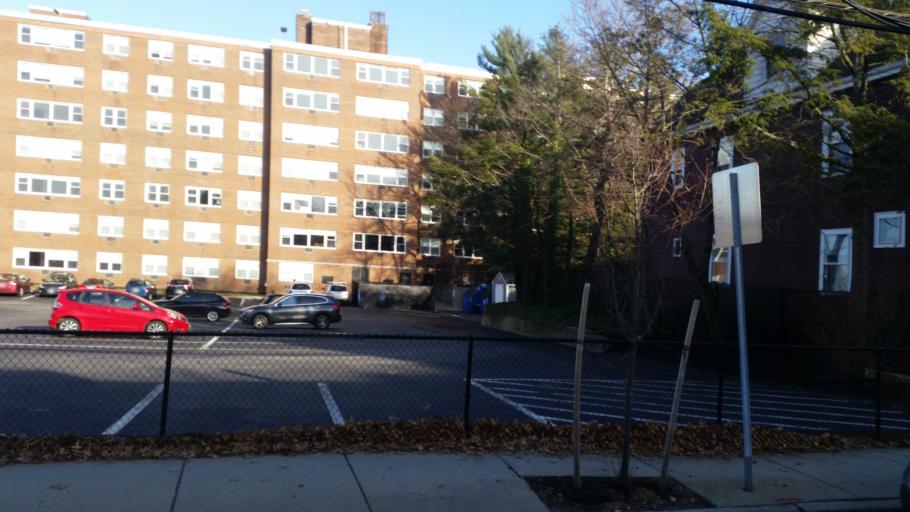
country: US
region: Massachusetts
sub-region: Middlesex County
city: Cambridge
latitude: 42.3866
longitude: -71.1313
